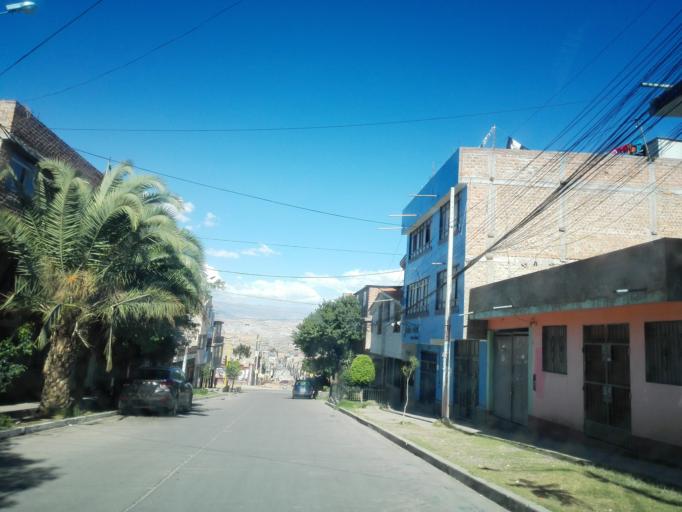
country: PE
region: Ayacucho
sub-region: Provincia de Huamanga
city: Ayacucho
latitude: -13.1555
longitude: -74.2286
